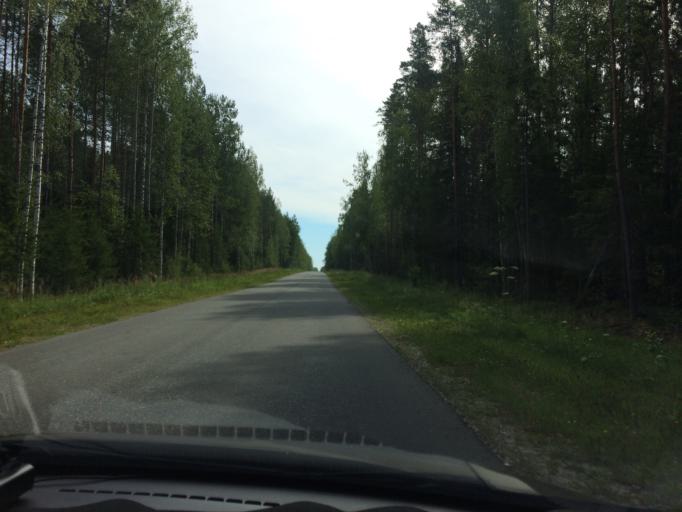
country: RU
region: Mariy-El
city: Mochalishche
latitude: 56.5480
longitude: 48.3433
